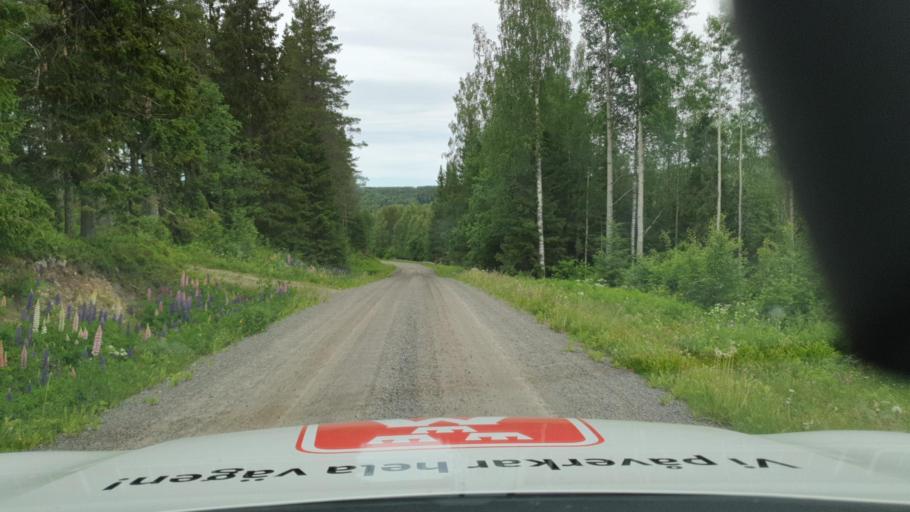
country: SE
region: Vaesterbotten
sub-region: Skelleftea Kommun
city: Burtraesk
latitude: 64.3880
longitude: 20.6125
